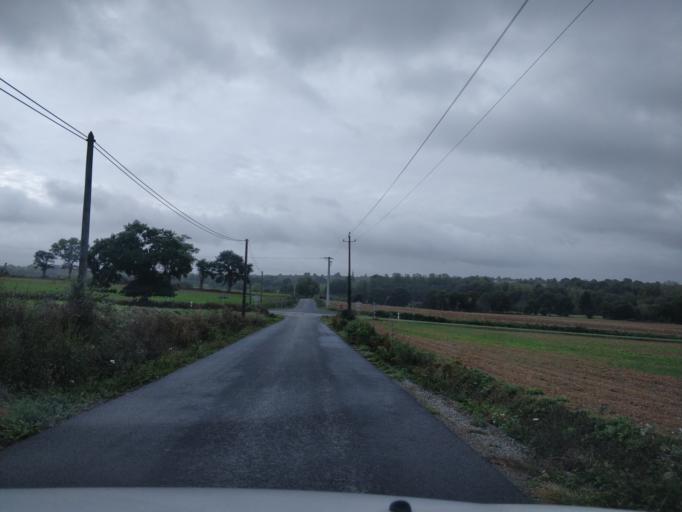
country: FR
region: Brittany
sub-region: Departement d'Ille-et-Vilaine
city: La Bouexiere
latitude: 48.1982
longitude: -1.4356
